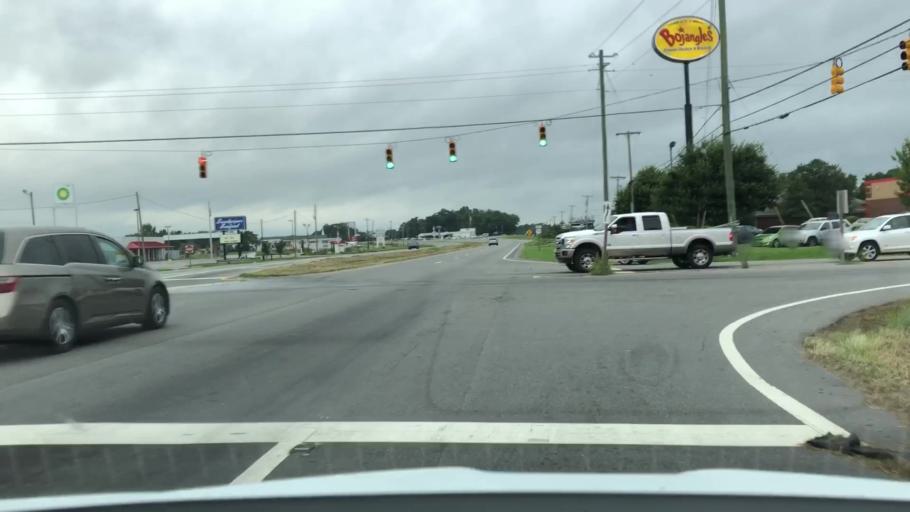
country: US
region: North Carolina
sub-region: Lenoir County
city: La Grange
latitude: 35.2861
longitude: -77.7567
